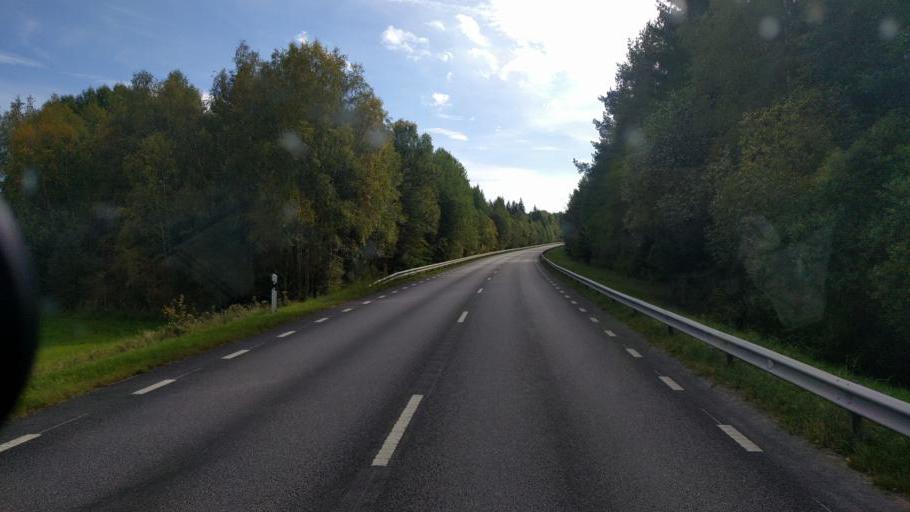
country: SE
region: OEstergoetland
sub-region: Kinda Kommun
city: Kisa
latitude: 57.9485
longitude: 15.6656
